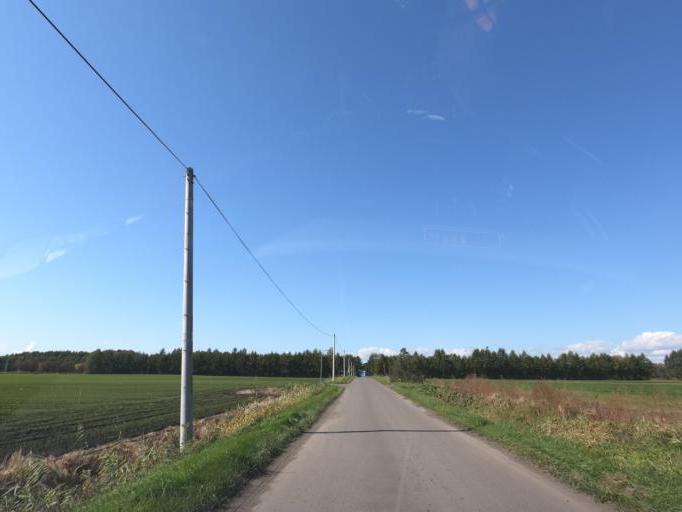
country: JP
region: Hokkaido
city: Otofuke
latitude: 43.0705
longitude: 143.2695
